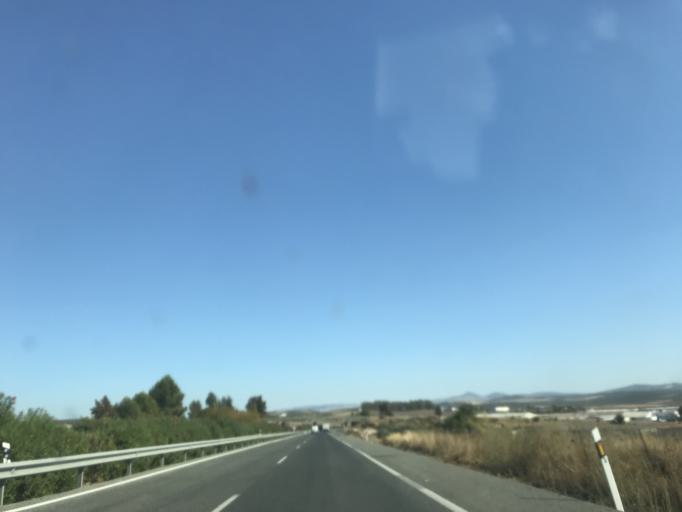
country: ES
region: Andalusia
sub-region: Provincia de Sevilla
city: La Puebla de Cazalla
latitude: 37.2330
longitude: -5.3055
